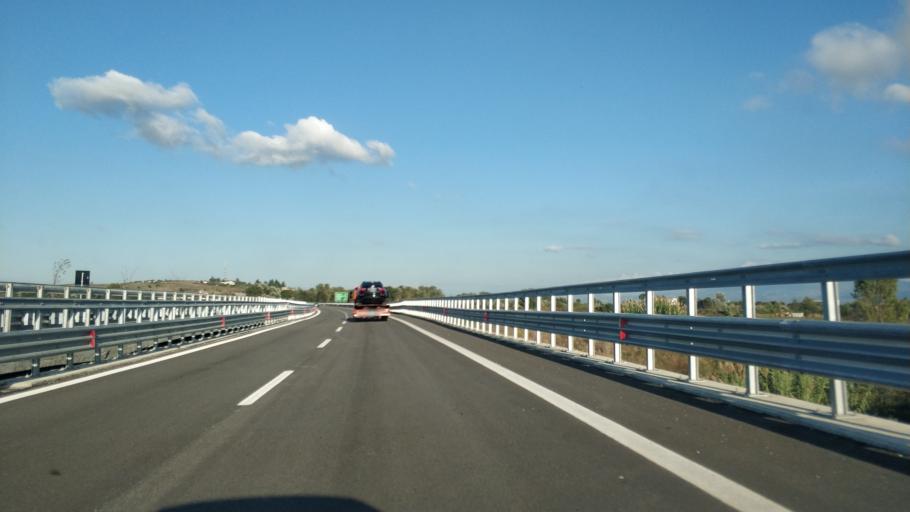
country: AL
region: Fier
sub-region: Rrethi i Fierit
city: Mbrostar-Ure
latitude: 40.7484
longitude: 19.5641
